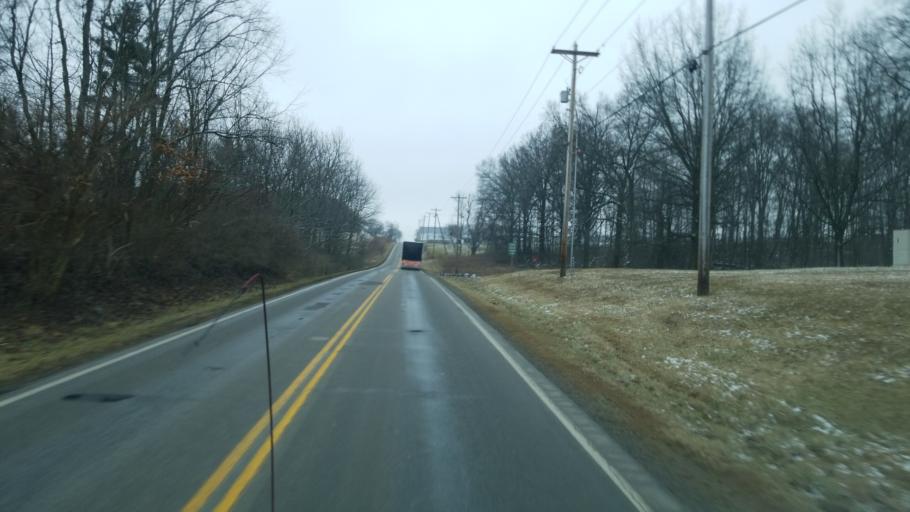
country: US
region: Ohio
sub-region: Wayne County
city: Apple Creek
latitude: 40.7683
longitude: -81.8439
